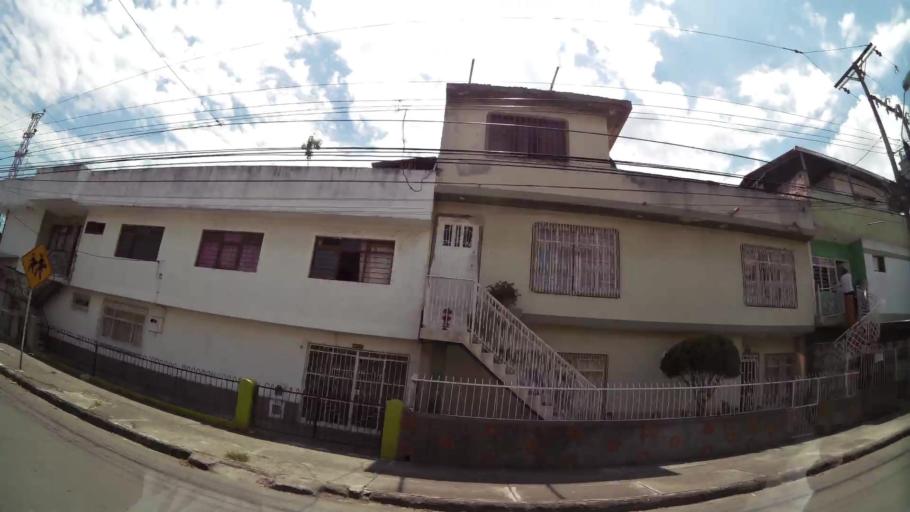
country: CO
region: Valle del Cauca
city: Cali
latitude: 3.4374
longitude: -76.5155
